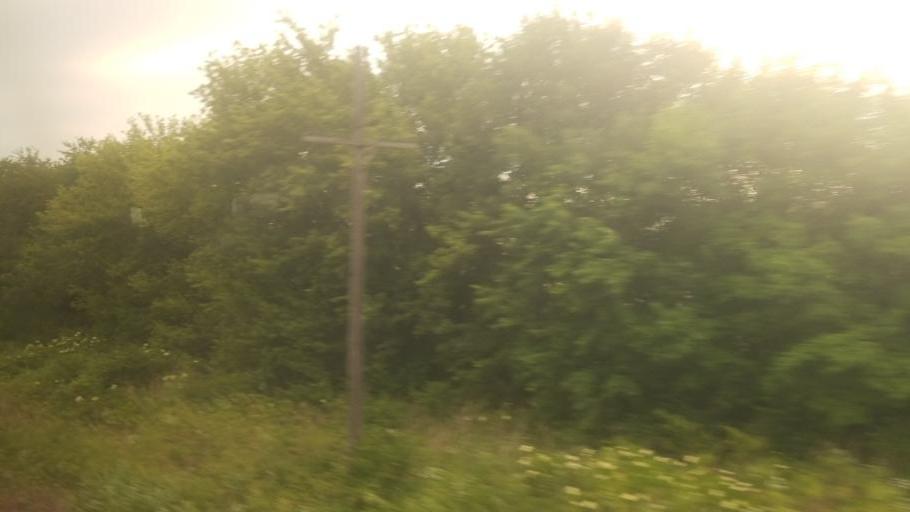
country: US
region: Kansas
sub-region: Shawnee County
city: Topeka
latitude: 38.9667
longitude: -95.6880
